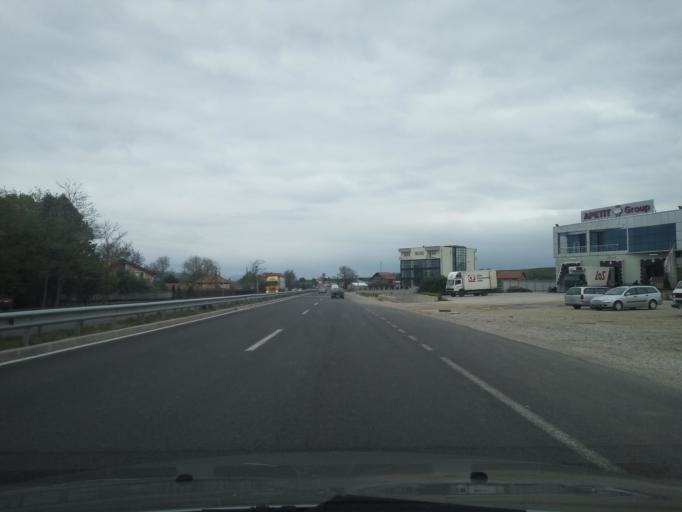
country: XK
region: Pristina
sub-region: Komuna e Obiliqit
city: Obiliq
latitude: 42.7339
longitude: 21.0694
